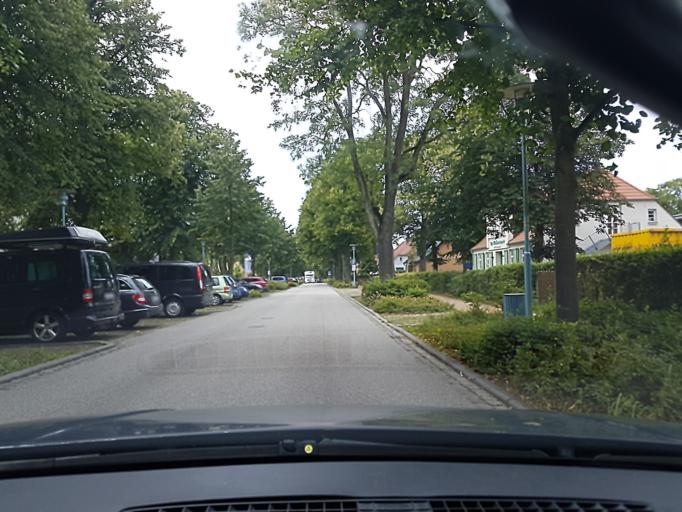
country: DE
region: Mecklenburg-Vorpommern
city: Ostseebad Dierhagen
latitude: 54.3491
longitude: 12.3957
